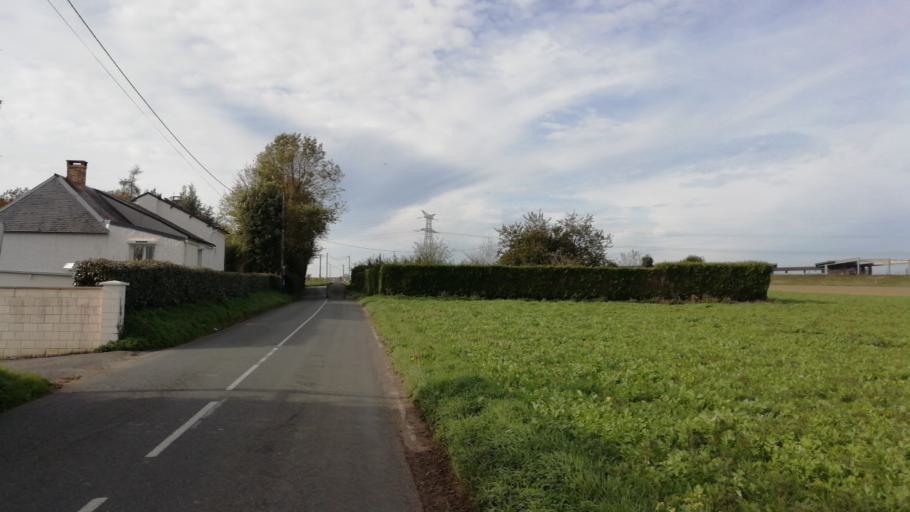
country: FR
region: Haute-Normandie
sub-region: Departement de la Seine-Maritime
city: Saint-Martin-du-Manoir
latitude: 49.5384
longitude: 0.2219
